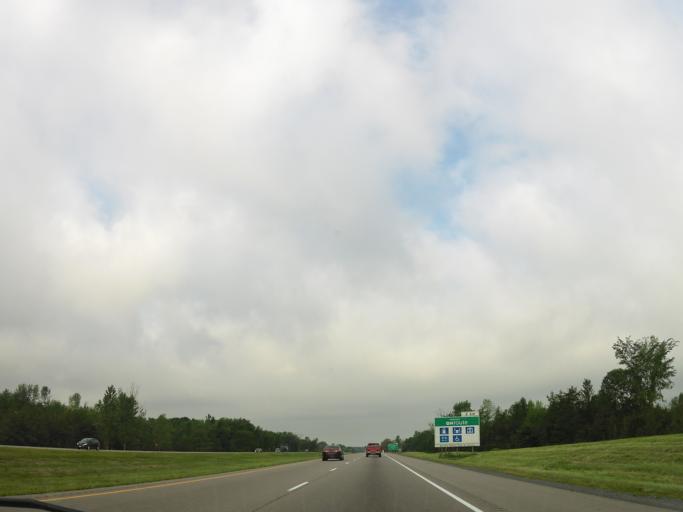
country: CA
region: Ontario
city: Skatepark
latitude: 44.2802
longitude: -76.7657
